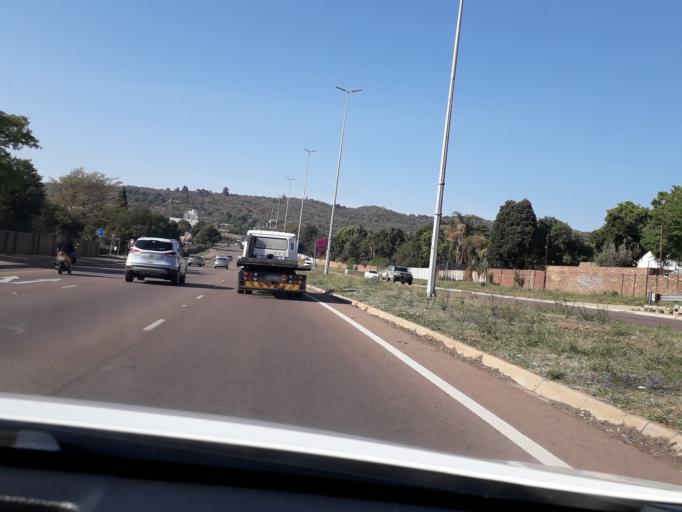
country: ZA
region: Gauteng
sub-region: City of Tshwane Metropolitan Municipality
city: Pretoria
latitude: -25.7601
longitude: 28.3232
